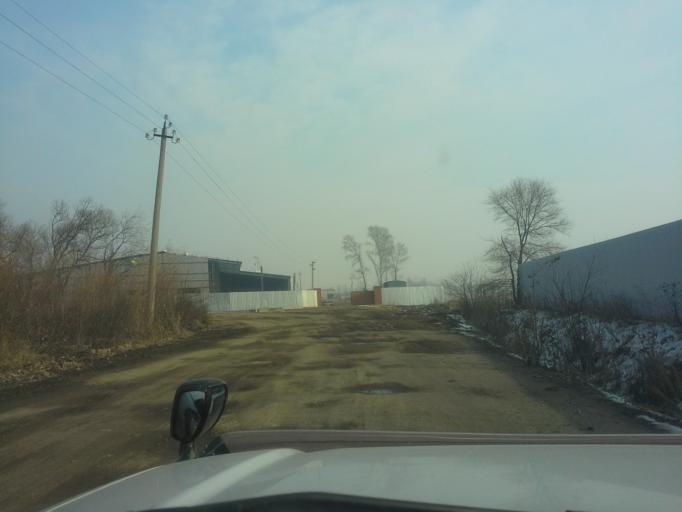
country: RU
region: Jewish Autonomous Oblast
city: Priamurskiy
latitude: 48.5336
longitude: 134.9030
